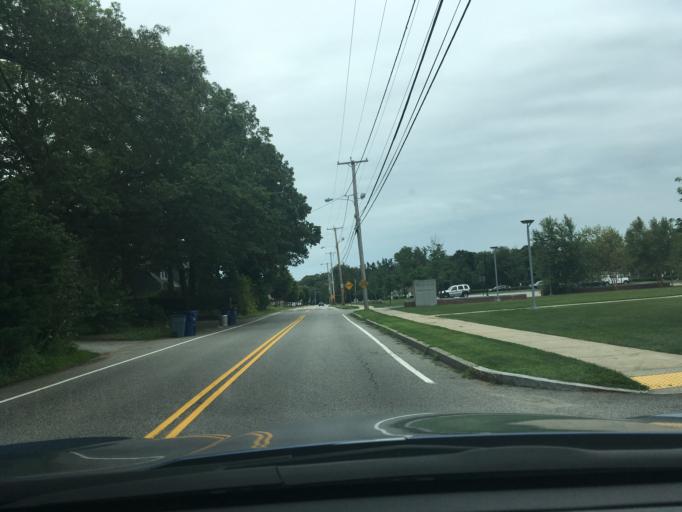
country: US
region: Rhode Island
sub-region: Kent County
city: East Greenwich
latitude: 41.6525
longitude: -71.4620
